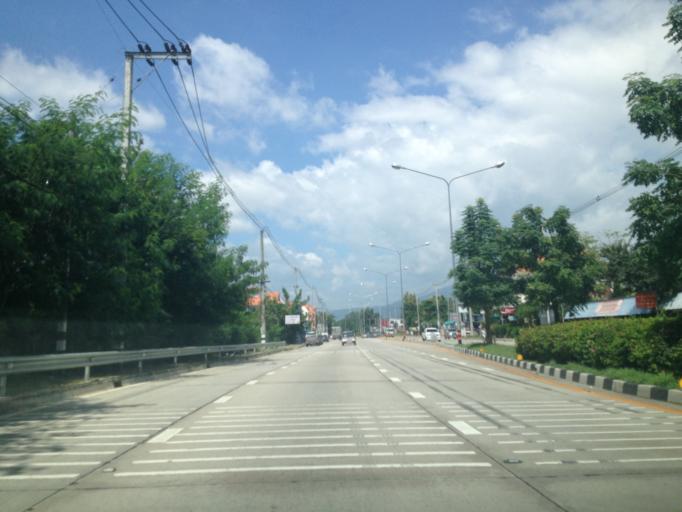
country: TH
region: Chiang Mai
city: Saraphi
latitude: 18.7423
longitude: 99.0003
